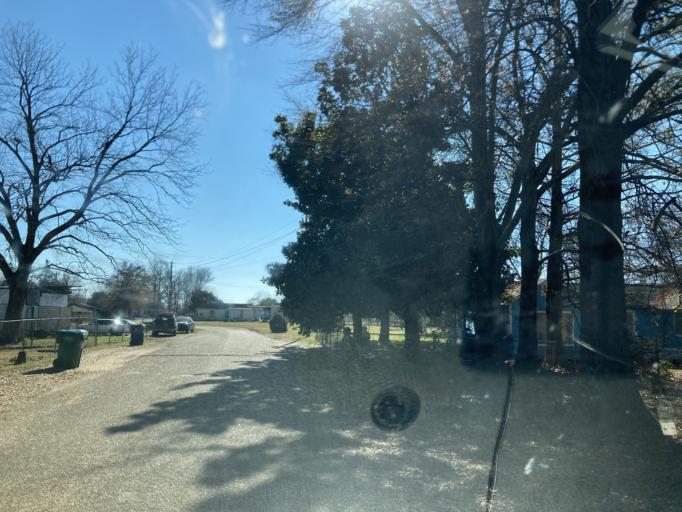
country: US
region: Mississippi
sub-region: Yazoo County
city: Yazoo City
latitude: 32.9774
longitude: -90.5931
